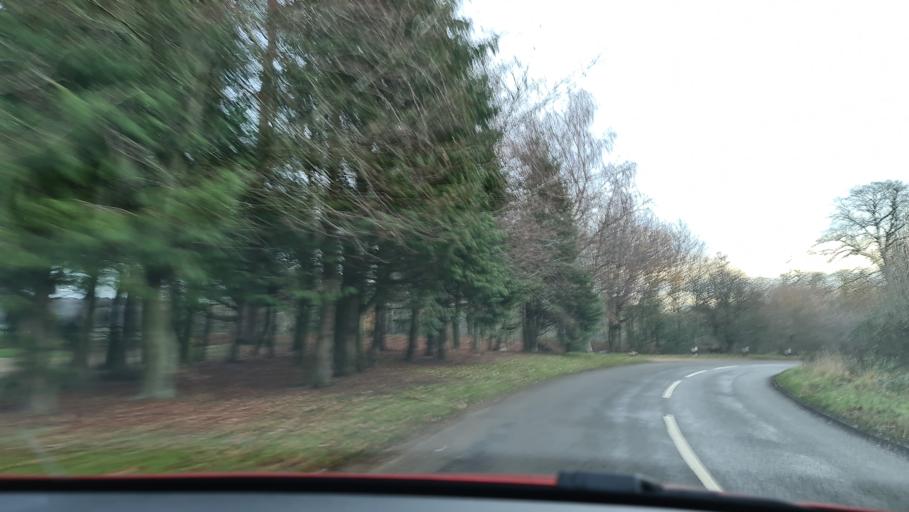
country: GB
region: England
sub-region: Buckinghamshire
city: Wendover
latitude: 51.7119
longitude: -0.7694
